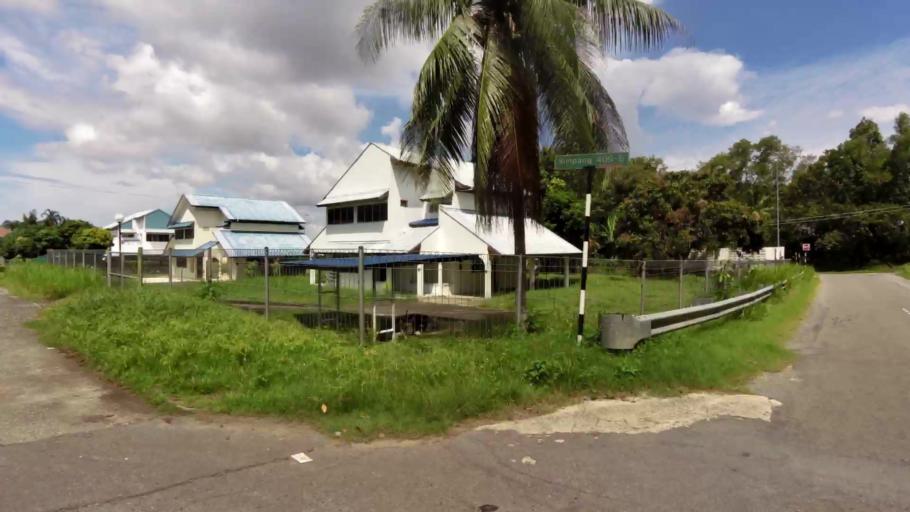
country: BN
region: Brunei and Muara
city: Bandar Seri Begawan
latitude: 4.9791
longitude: 114.9483
